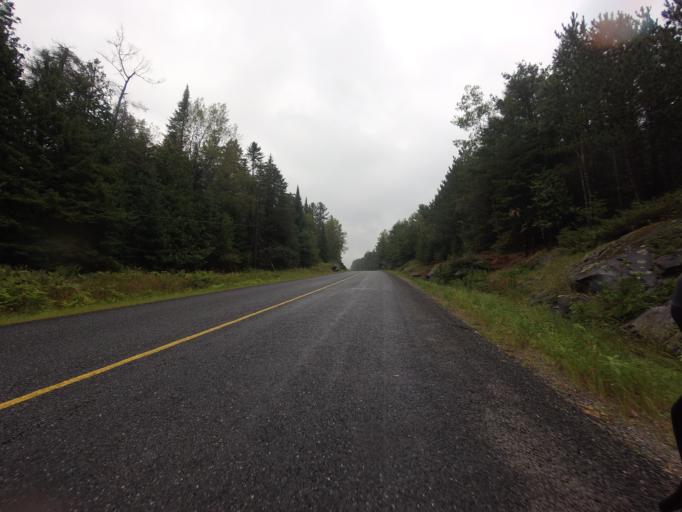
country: CA
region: Ontario
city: Perth
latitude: 45.0781
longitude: -76.4839
